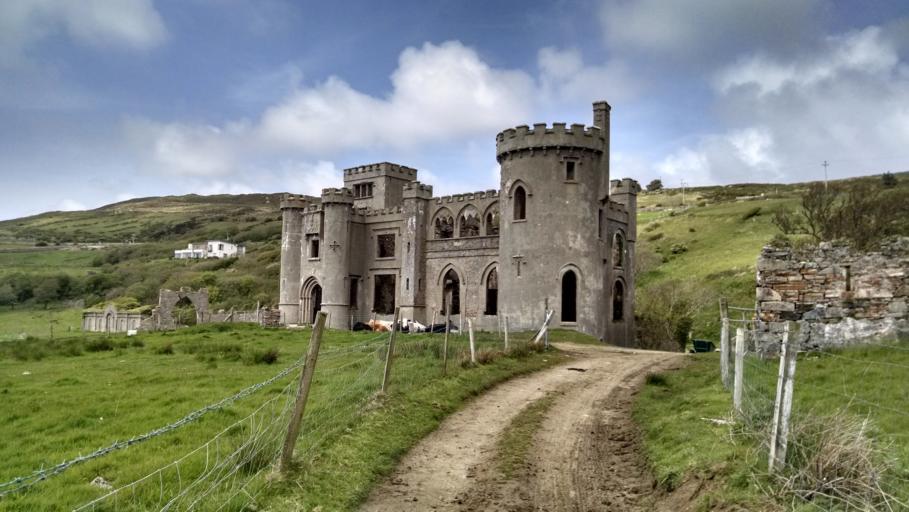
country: IE
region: Connaught
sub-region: County Galway
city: Clifden
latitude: 53.4913
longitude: -10.0564
